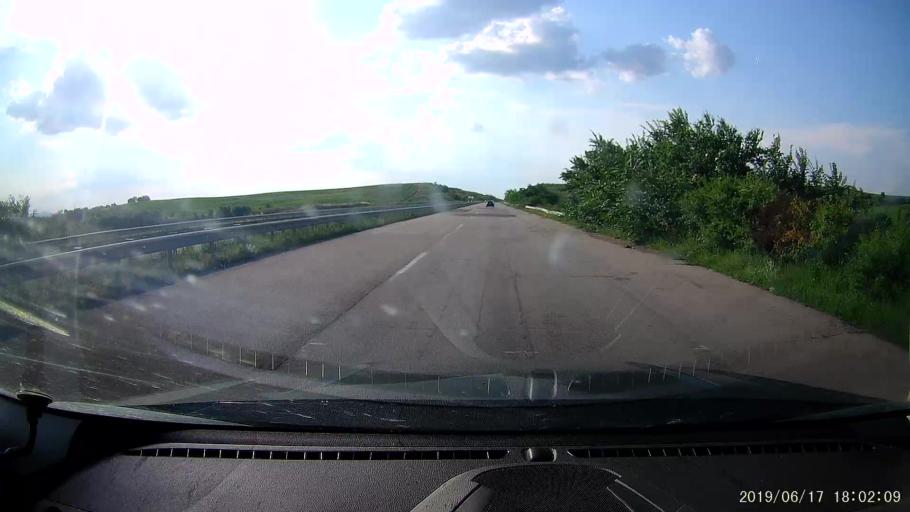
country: BG
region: Khaskovo
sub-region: Obshtina Svilengrad
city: Svilengrad
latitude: 41.7547
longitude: 26.2364
